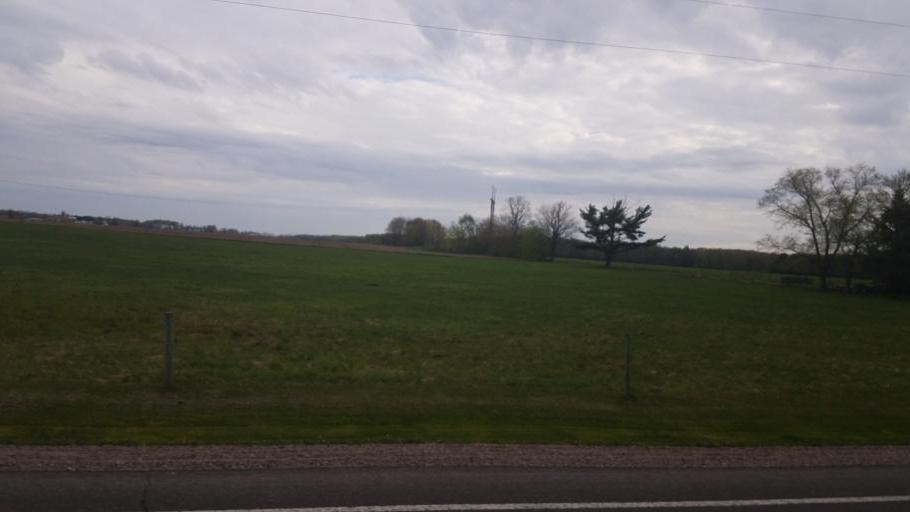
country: US
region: Wisconsin
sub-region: Marathon County
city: Spencer
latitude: 44.6552
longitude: -90.3733
